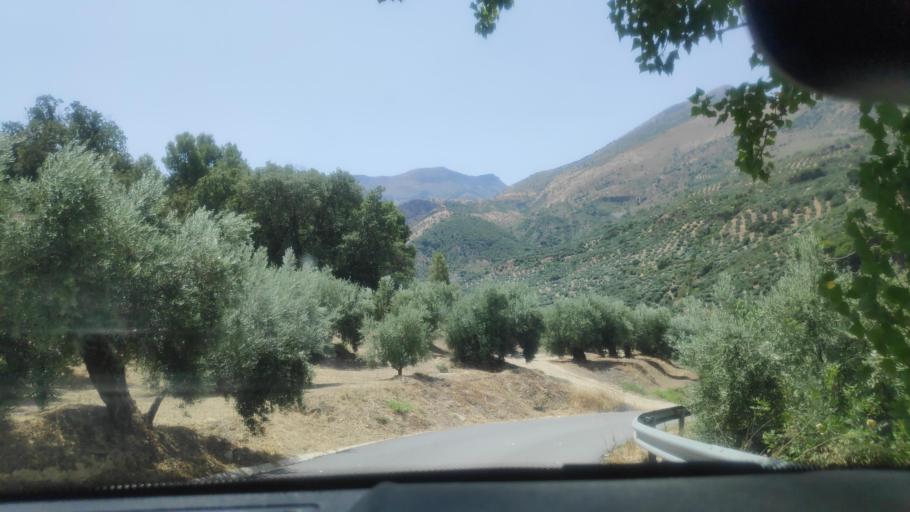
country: ES
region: Andalusia
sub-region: Provincia de Jaen
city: Torres
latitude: 37.7883
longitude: -3.4551
